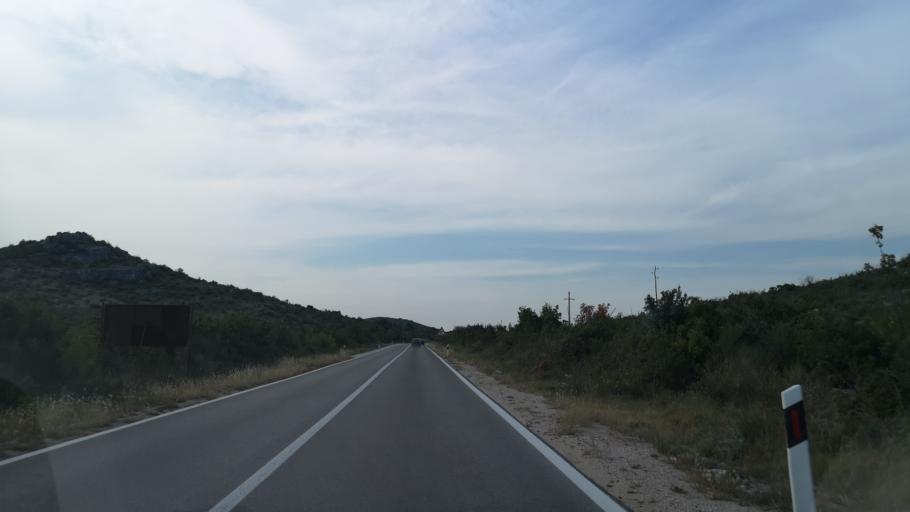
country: HR
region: Sibensko-Kniniska
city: Zaton
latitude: 43.8288
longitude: 15.7798
